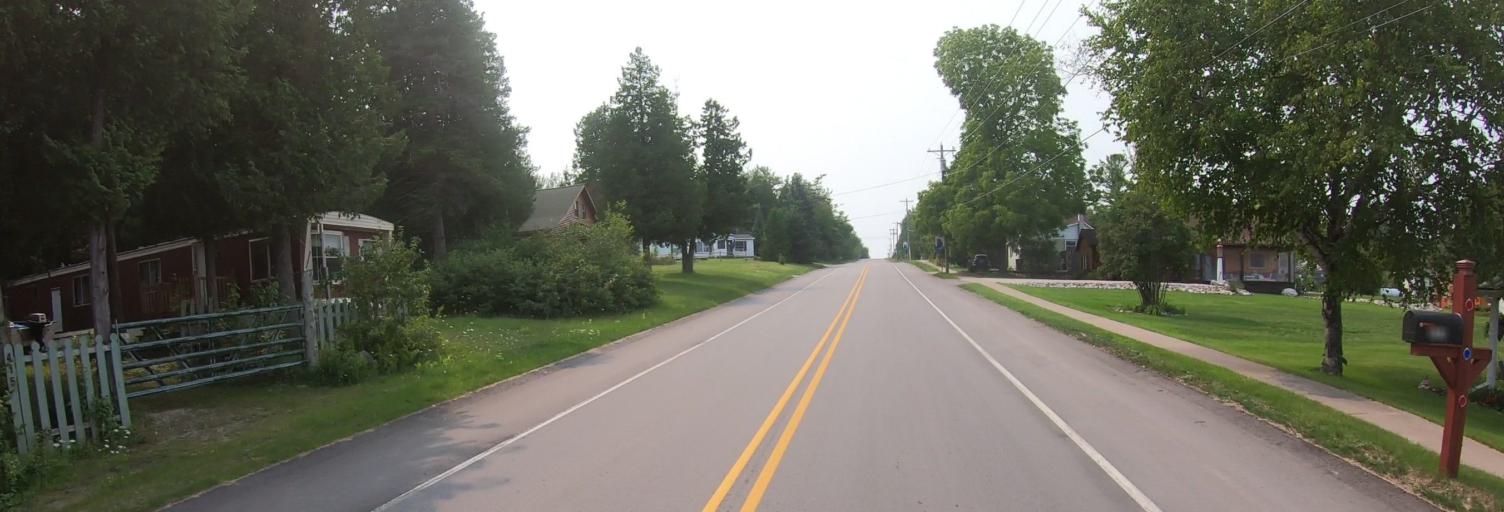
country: CA
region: Ontario
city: Thessalon
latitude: 45.9997
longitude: -83.9029
